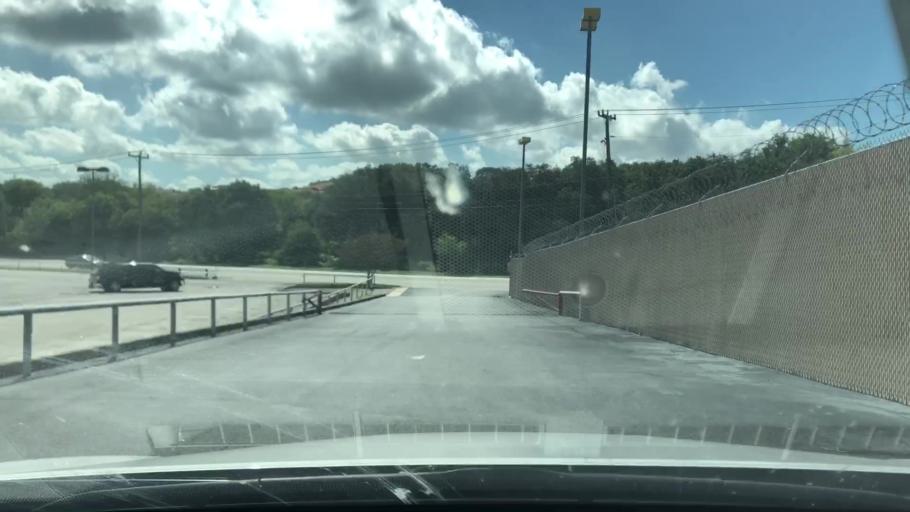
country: US
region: Texas
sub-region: Bexar County
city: Live Oak
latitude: 29.5514
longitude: -98.3530
